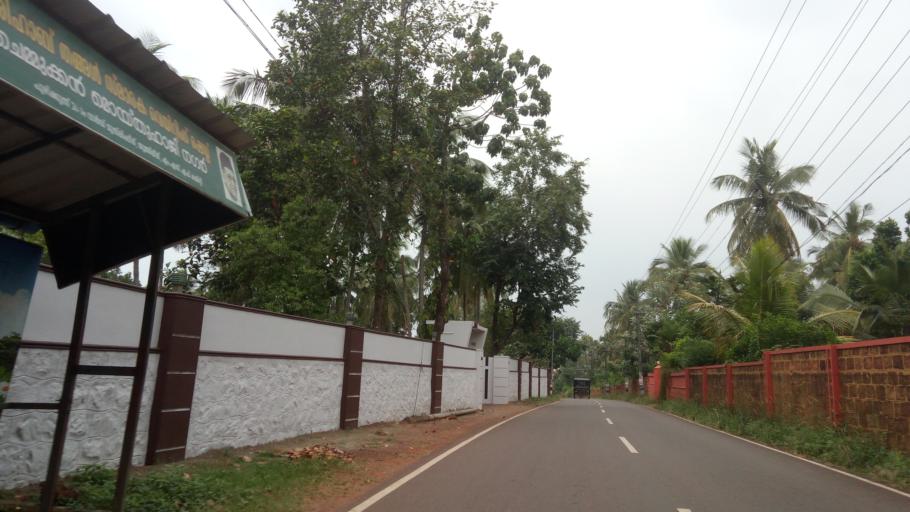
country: IN
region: Kerala
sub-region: Malappuram
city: Malappuram
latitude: 10.9824
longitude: 76.0065
